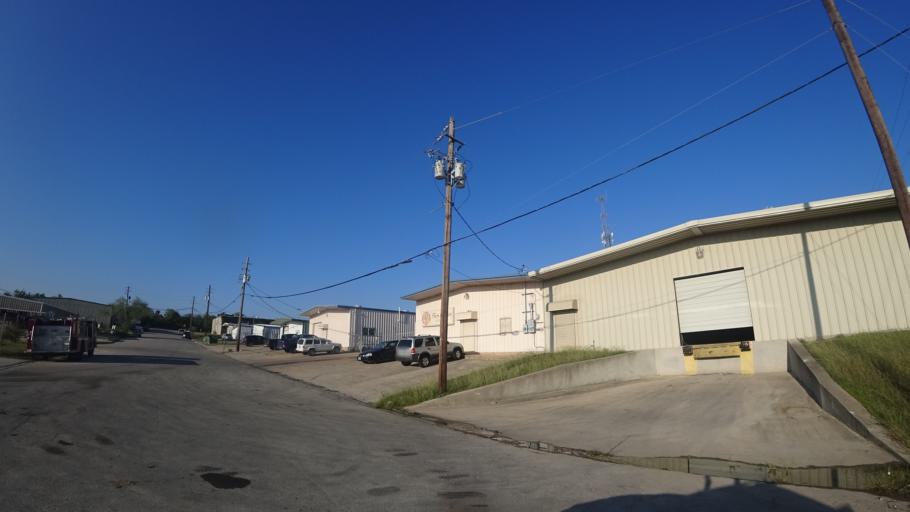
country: US
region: Texas
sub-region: Travis County
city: Austin
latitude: 30.3238
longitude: -97.6618
